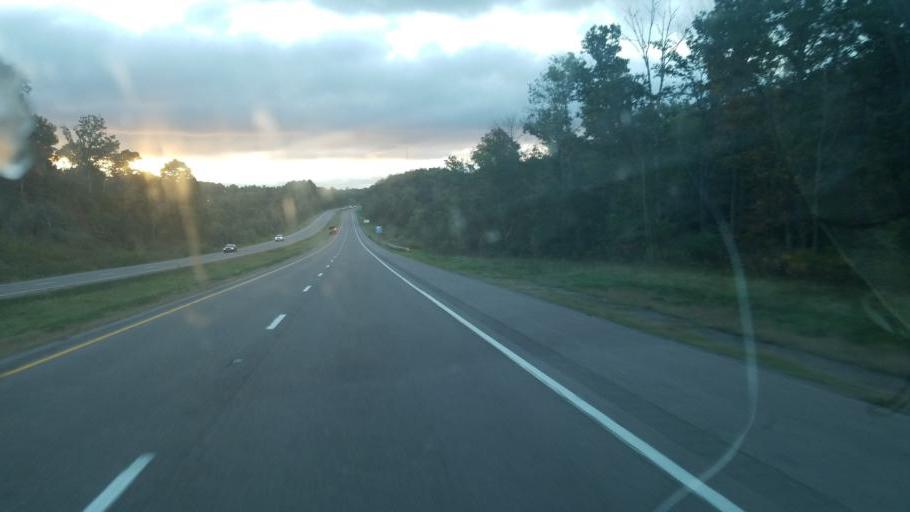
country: US
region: West Virginia
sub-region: Preston County
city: Terra Alta
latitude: 39.6591
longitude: -79.4581
